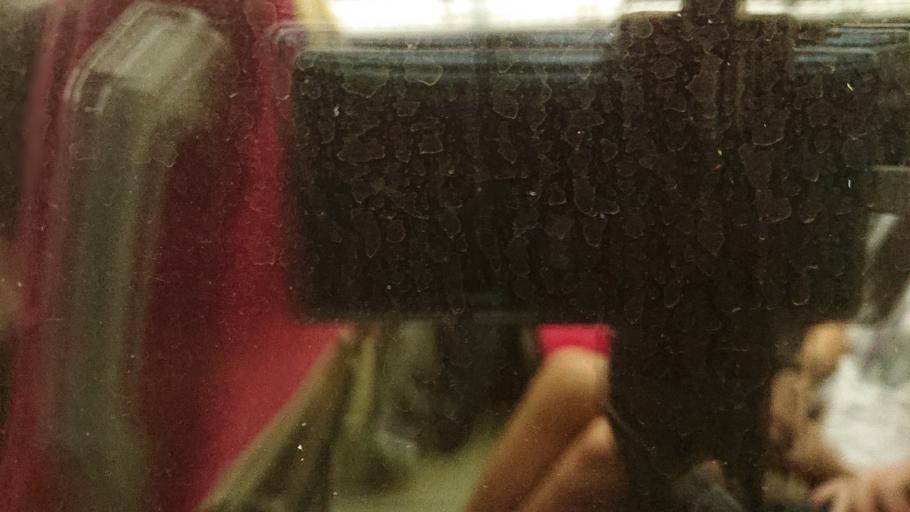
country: TW
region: Taiwan
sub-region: Yilan
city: Yilan
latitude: 24.9448
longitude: 121.8999
